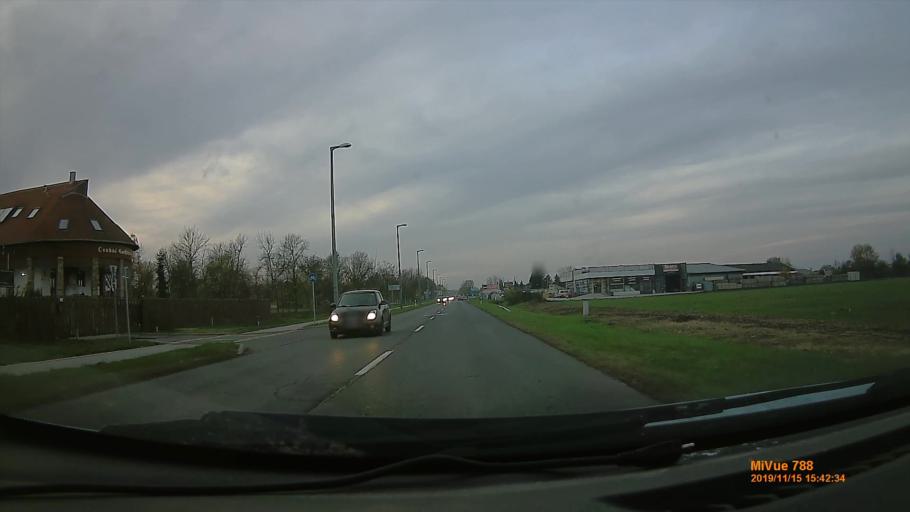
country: HU
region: Bekes
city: Bekescsaba
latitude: 46.6782
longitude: 21.1244
